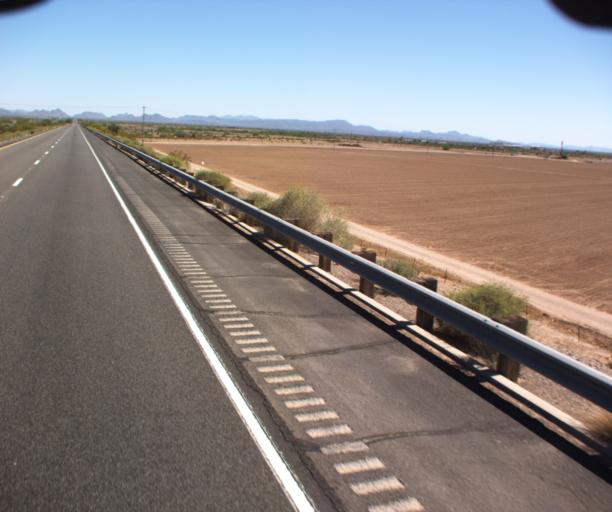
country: US
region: Arizona
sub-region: Maricopa County
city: Gila Bend
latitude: 32.9415
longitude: -112.7397
